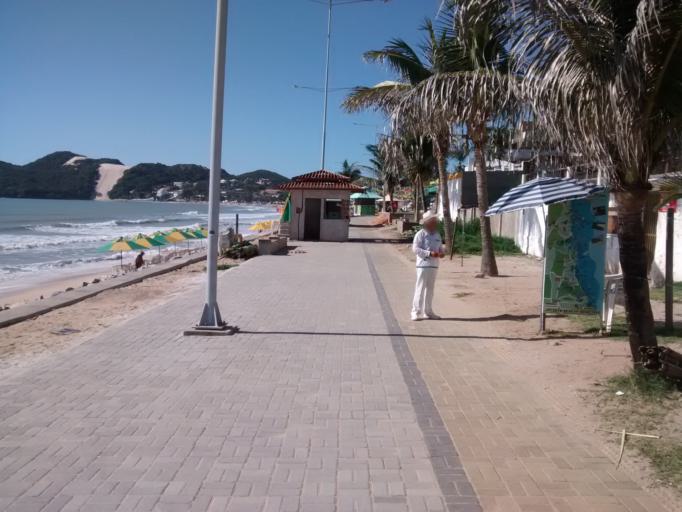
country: BR
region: Rio Grande do Norte
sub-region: Natal
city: Natal
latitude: -5.8773
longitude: -35.1747
